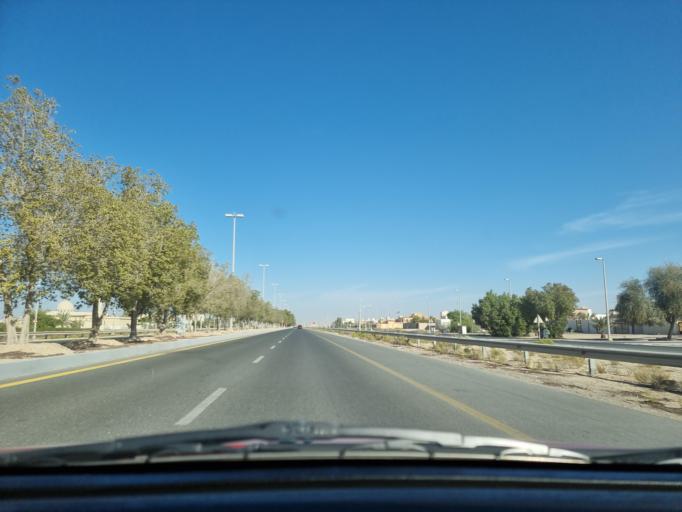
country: AE
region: Abu Dhabi
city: Abu Dhabi
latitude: 24.3892
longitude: 54.6950
